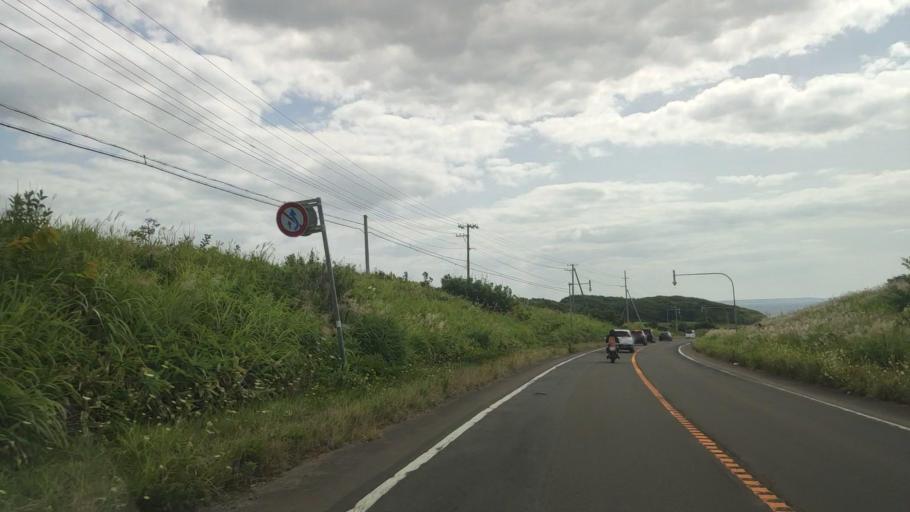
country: JP
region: Hokkaido
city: Rumoi
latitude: 44.5135
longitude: 141.7665
